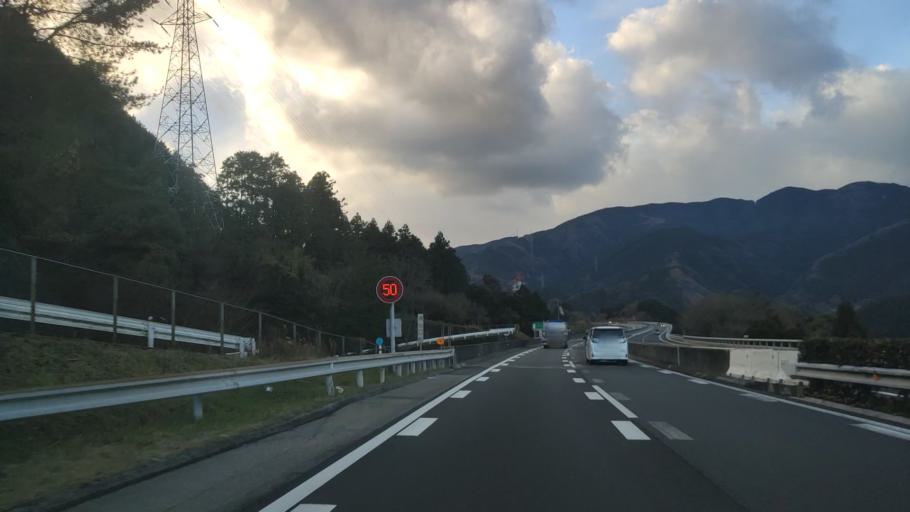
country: JP
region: Ehime
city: Saijo
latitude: 33.8532
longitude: 133.0138
